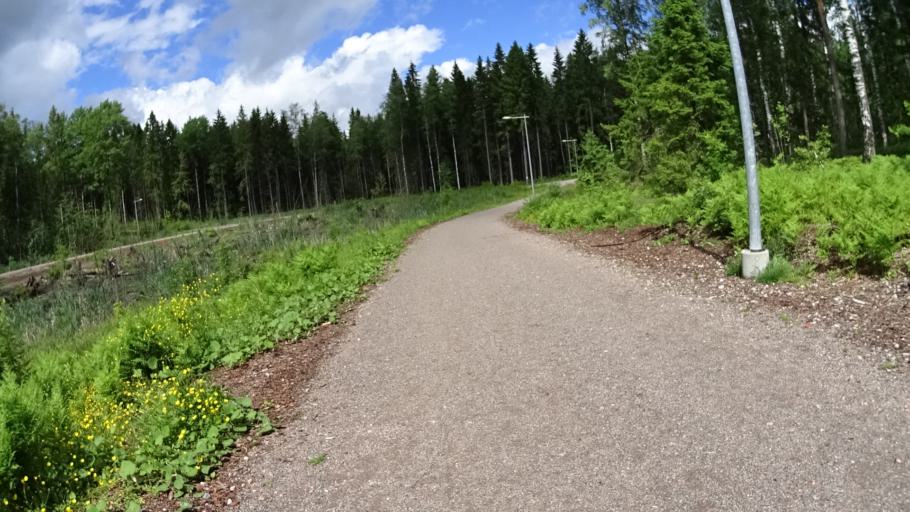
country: FI
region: Uusimaa
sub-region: Helsinki
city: Kilo
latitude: 60.2429
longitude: 24.8246
